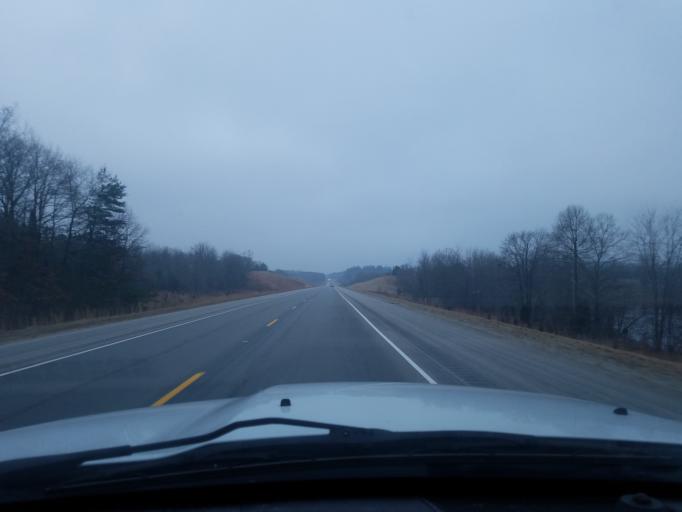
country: US
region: Indiana
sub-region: Perry County
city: Tell City
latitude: 38.1220
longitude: -86.6068
